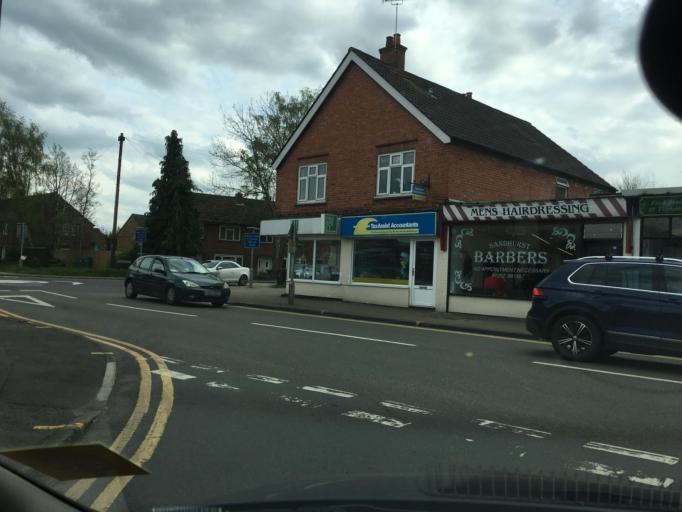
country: GB
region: England
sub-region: Bracknell Forest
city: Sandhurst
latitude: 51.3459
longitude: -0.8003
